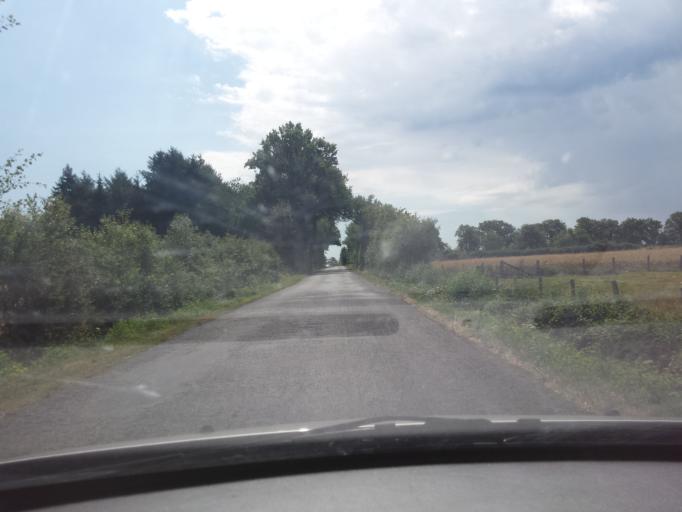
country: FR
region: Poitou-Charentes
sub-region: Departement de la Vienne
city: Availles-Limouzine
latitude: 46.0907
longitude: 0.7276
